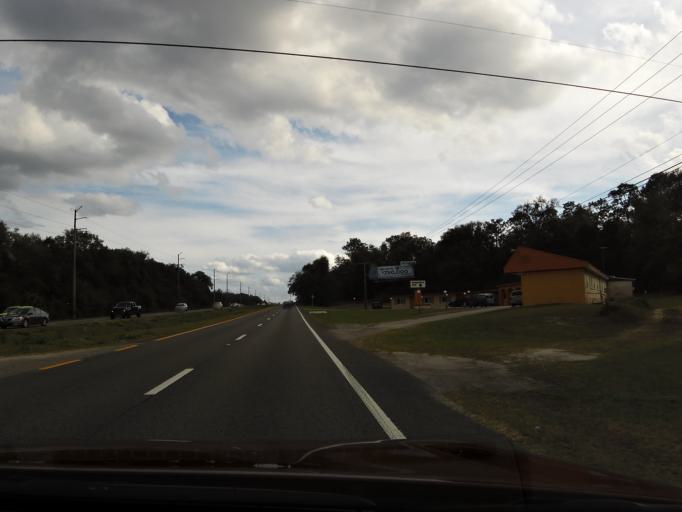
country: US
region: Florida
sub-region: Volusia County
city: De Leon Springs
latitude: 29.0963
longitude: -81.3340
